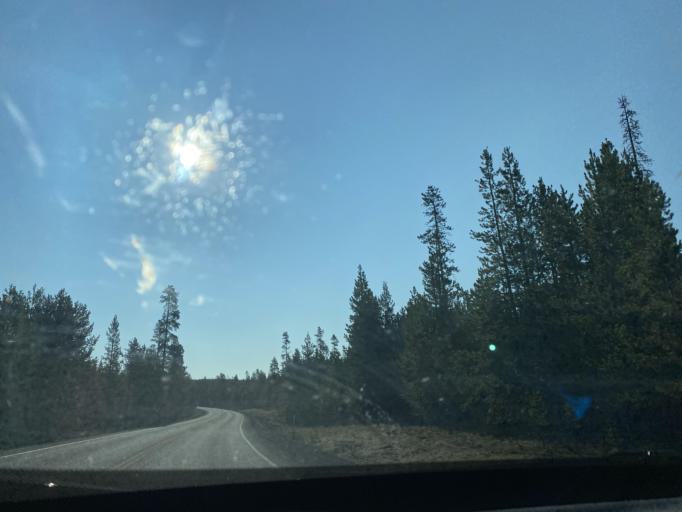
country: US
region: Oregon
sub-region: Deschutes County
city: Three Rivers
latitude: 43.7062
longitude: -121.2965
